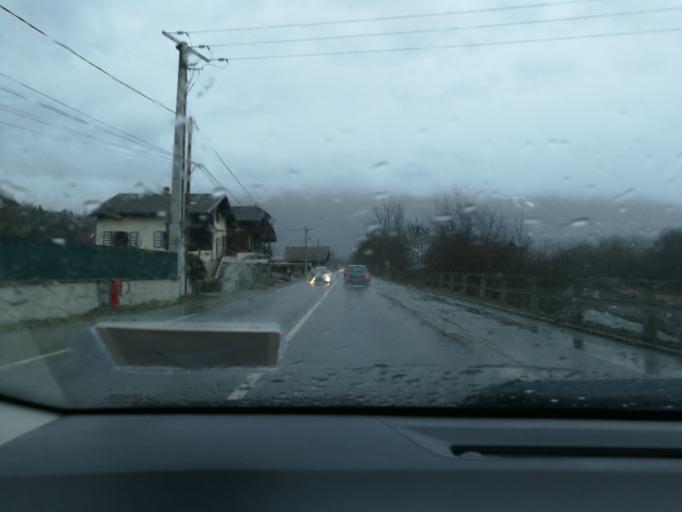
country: FR
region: Rhone-Alpes
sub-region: Departement de la Haute-Savoie
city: Passy
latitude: 45.9198
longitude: 6.6765
